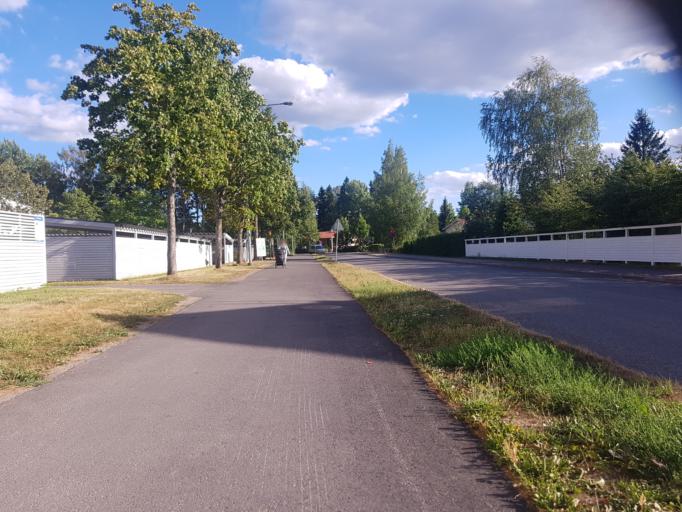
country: FI
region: Uusimaa
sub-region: Helsinki
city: Vantaa
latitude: 60.2740
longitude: 25.0021
